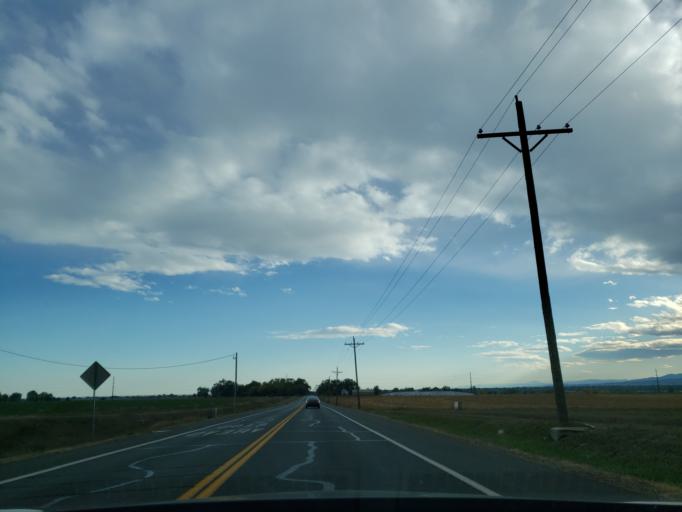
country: US
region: Colorado
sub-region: Larimer County
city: Fort Collins
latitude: 40.6089
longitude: -105.0293
